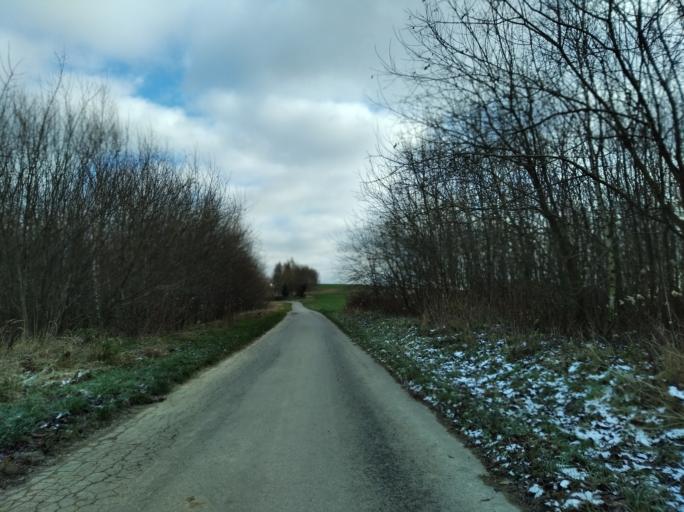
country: PL
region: Subcarpathian Voivodeship
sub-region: Powiat strzyzowski
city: Strzyzow
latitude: 49.8836
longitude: 21.8441
